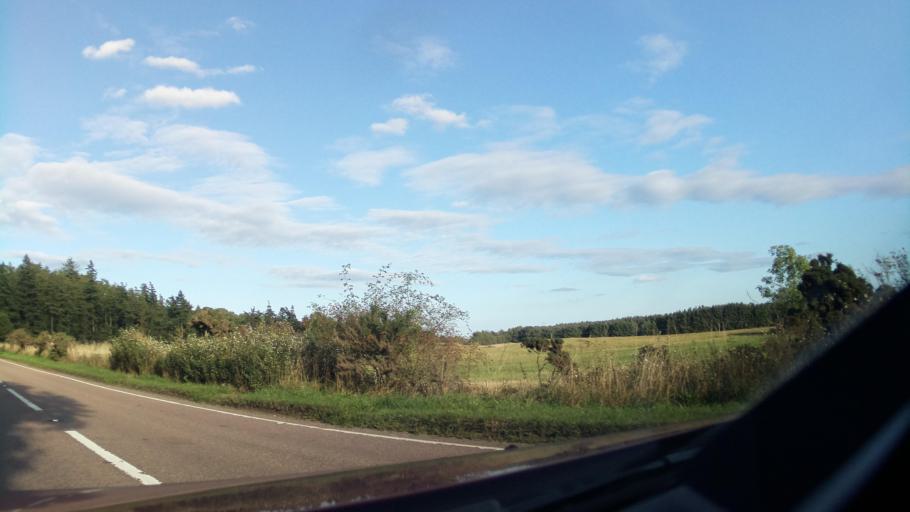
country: GB
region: Scotland
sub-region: Fife
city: Newport-On-Tay
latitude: 56.4084
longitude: -2.9510
